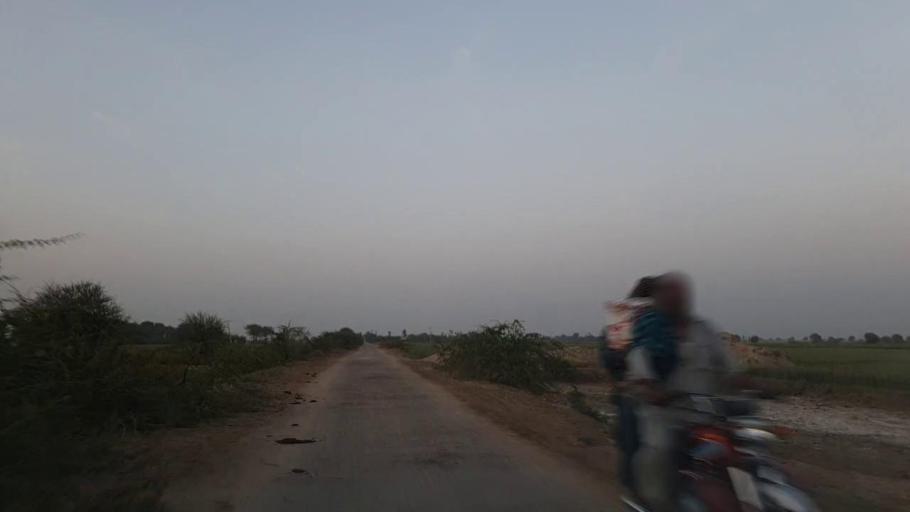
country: PK
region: Sindh
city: Naukot
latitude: 24.9917
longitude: 69.4245
